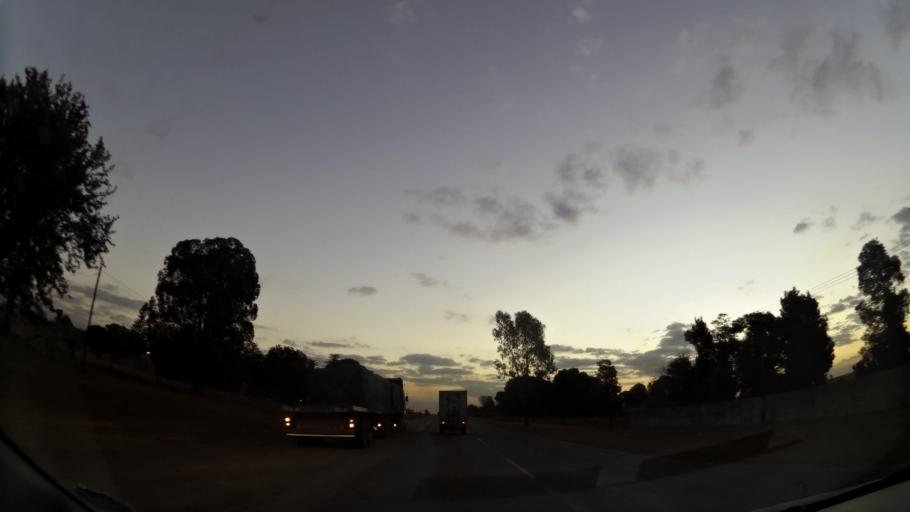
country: ZA
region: Gauteng
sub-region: West Rand District Municipality
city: Krugersdorp
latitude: -26.0701
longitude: 27.6759
